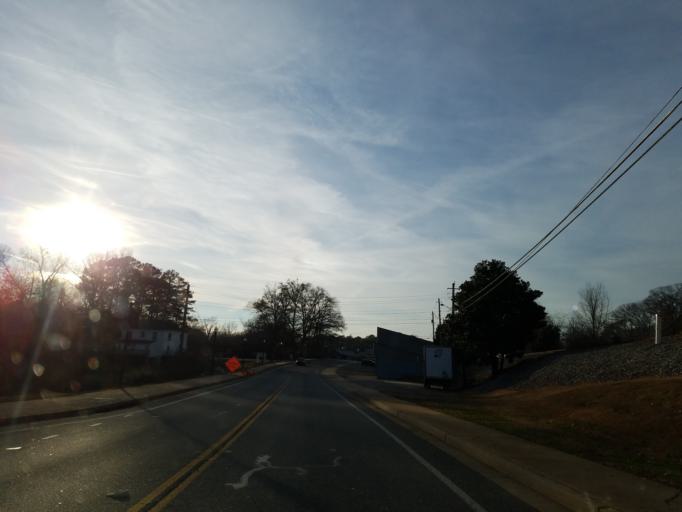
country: US
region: Georgia
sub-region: Cobb County
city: Acworth
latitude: 34.0642
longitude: -84.6696
